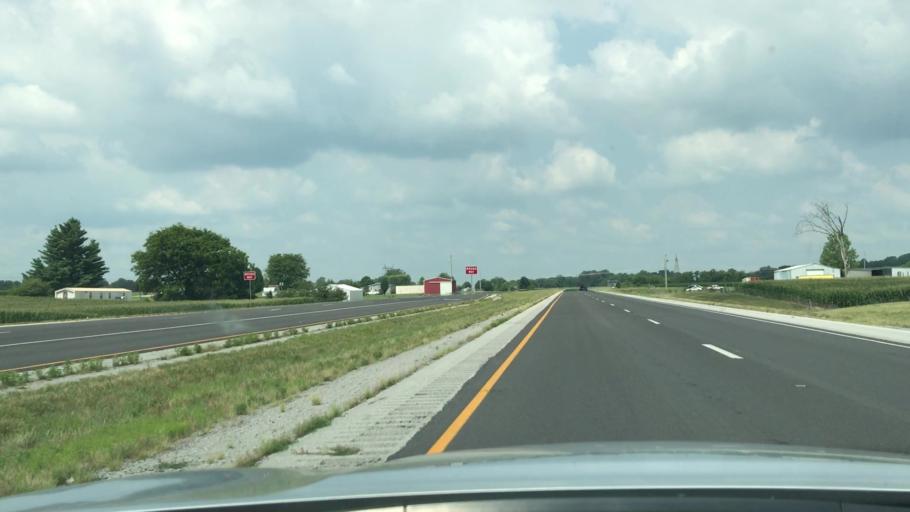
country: US
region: Kentucky
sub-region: Todd County
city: Elkton
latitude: 36.8029
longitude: -87.0951
